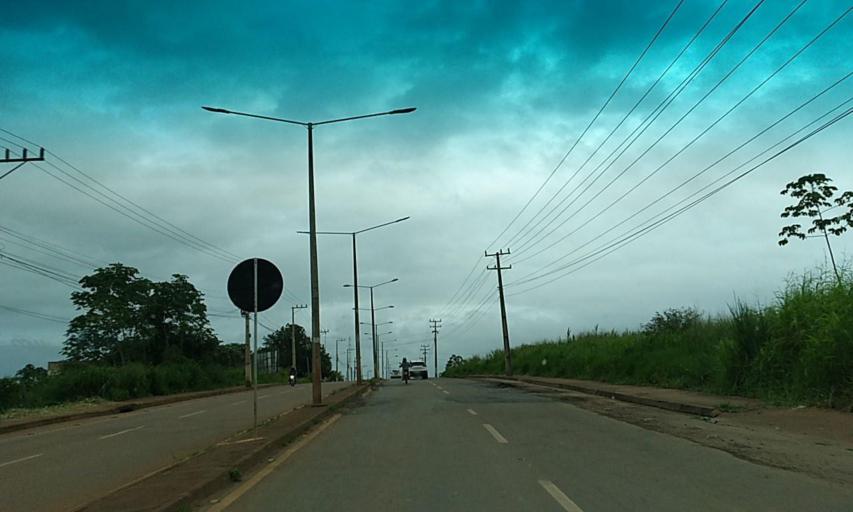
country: BR
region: Para
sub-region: Altamira
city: Altamira
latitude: -3.1870
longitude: -52.1896
